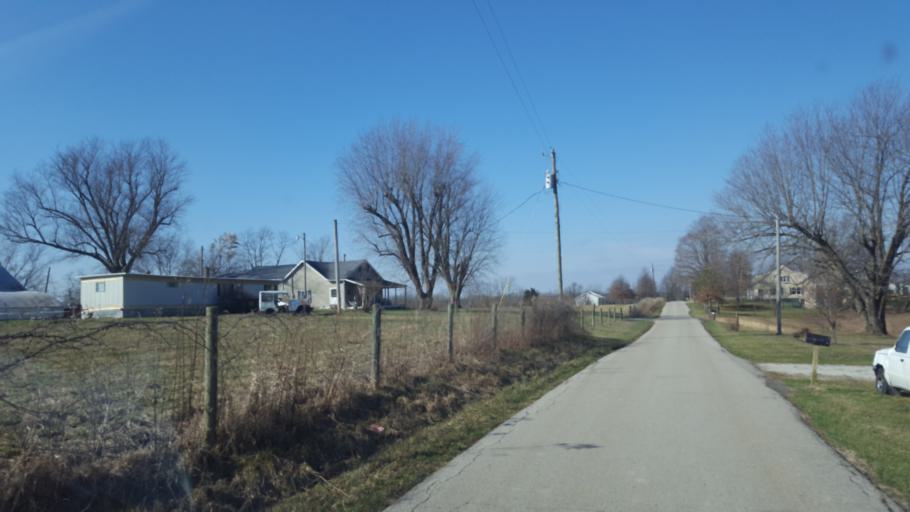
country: US
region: Kentucky
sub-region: Henry County
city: Eminence
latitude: 38.2979
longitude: -85.0332
